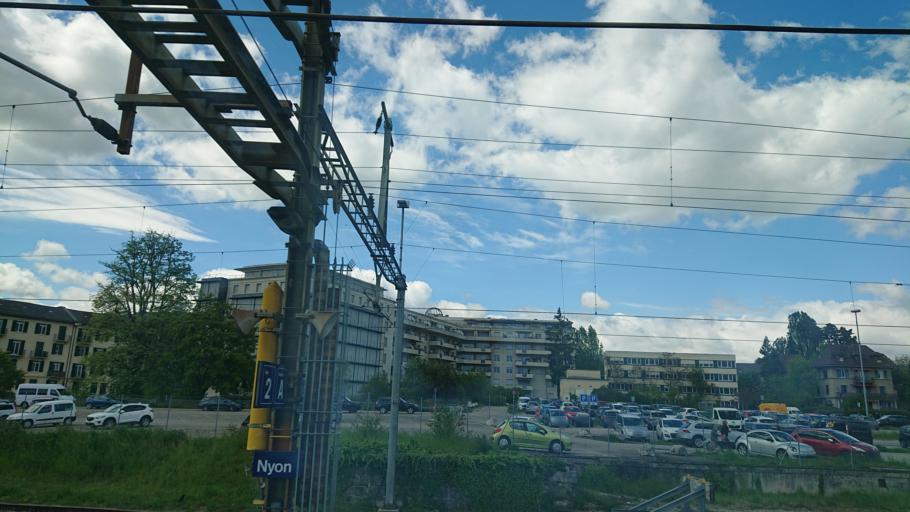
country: CH
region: Vaud
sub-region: Nyon District
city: Nyon
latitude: 46.3851
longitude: 6.2365
